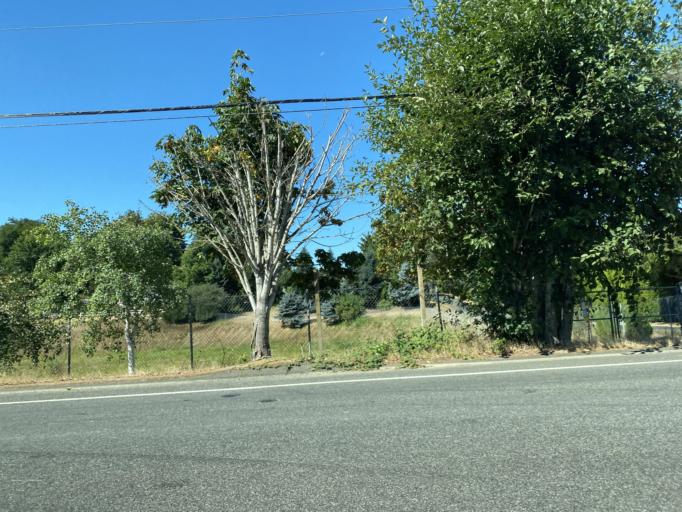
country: US
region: Washington
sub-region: Thurston County
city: Tumwater
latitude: 47.0078
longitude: -122.8652
